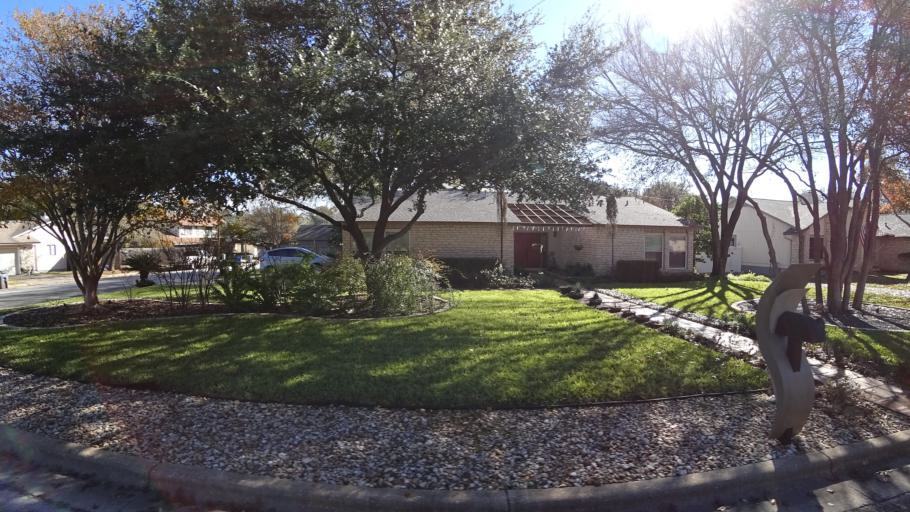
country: US
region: Texas
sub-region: Travis County
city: Wells Branch
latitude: 30.4256
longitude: -97.7114
